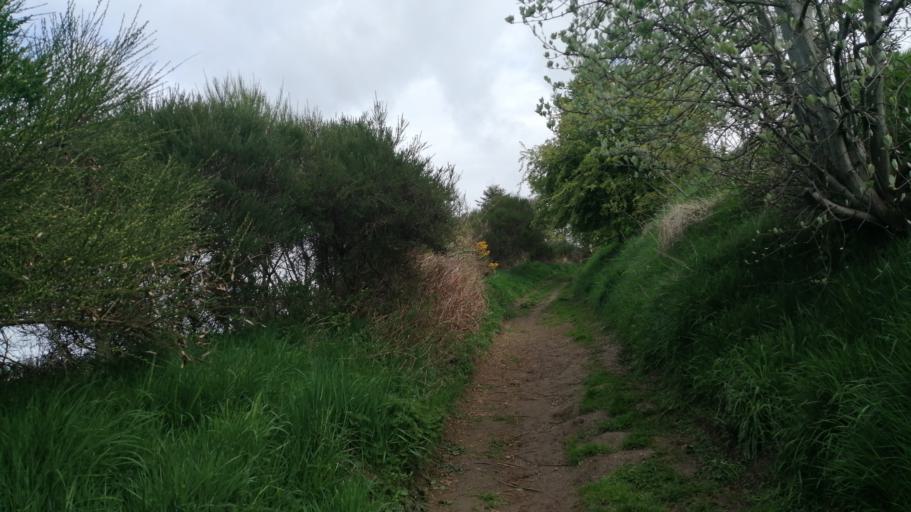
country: GB
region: Scotland
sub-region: Moray
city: Keith
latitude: 57.5356
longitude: -2.9601
